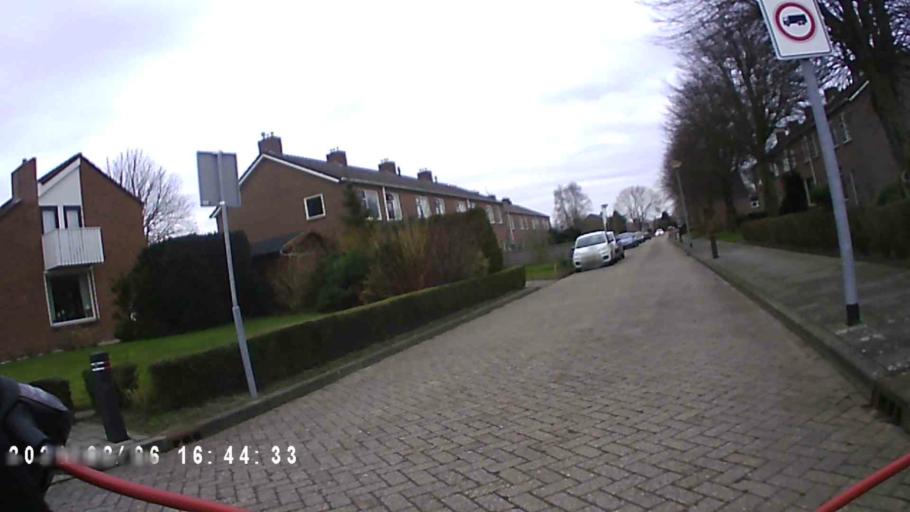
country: NL
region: Groningen
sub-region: Gemeente Appingedam
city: Appingedam
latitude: 53.4168
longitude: 6.7227
